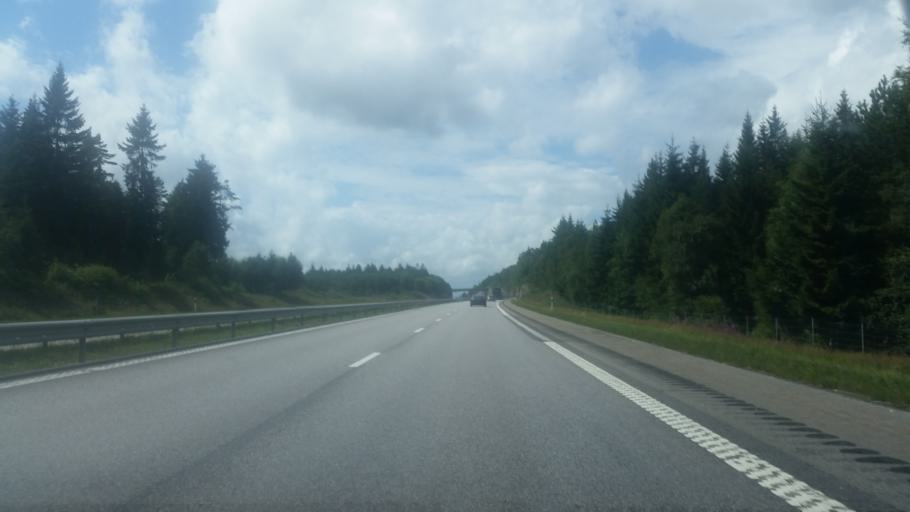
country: SE
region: Vaestra Goetaland
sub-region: Boras Kommun
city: Sandared
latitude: 57.6810
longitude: 12.7270
